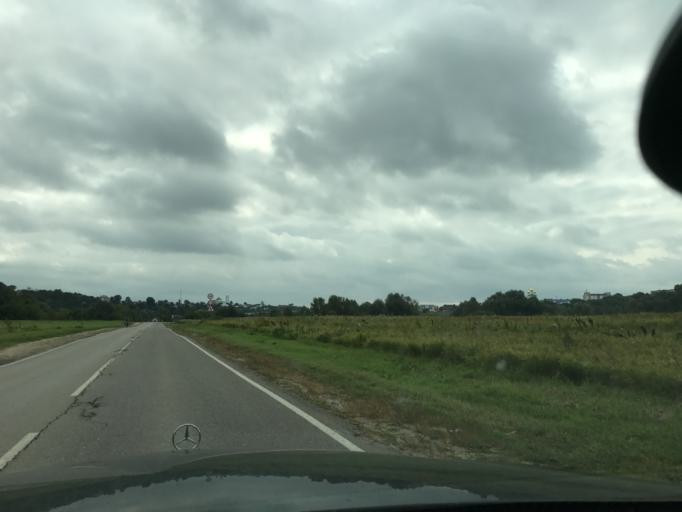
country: RU
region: Nizjnij Novgorod
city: Pavlovo
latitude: 55.9740
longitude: 43.0582
